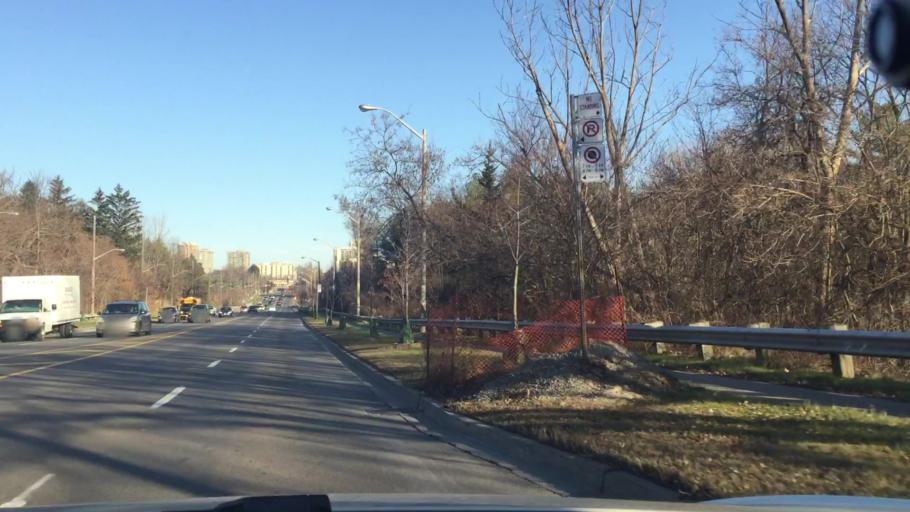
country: CA
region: Ontario
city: Willowdale
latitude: 43.7877
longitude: -79.3801
